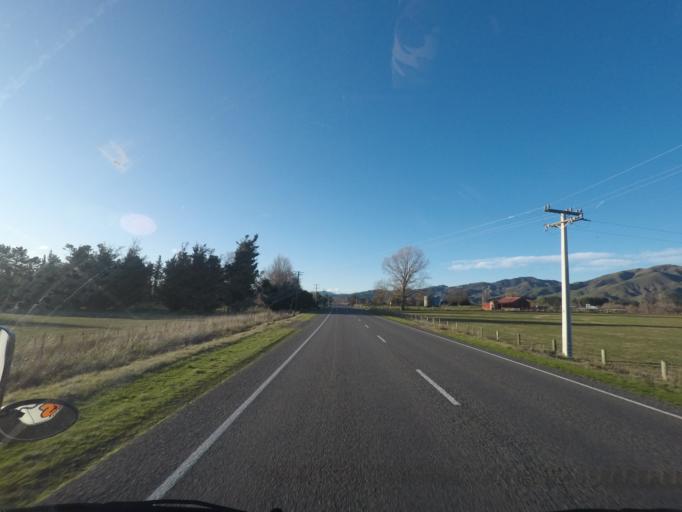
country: NZ
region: Canterbury
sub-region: Kaikoura District
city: Kaikoura
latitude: -42.7169
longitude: 173.2880
